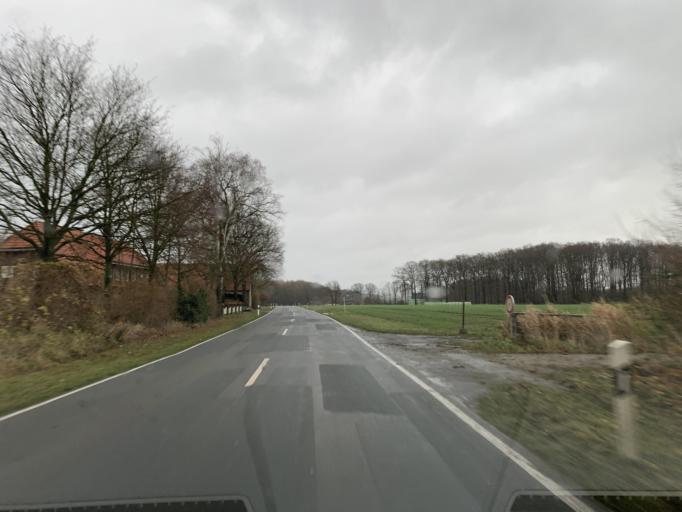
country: DE
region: North Rhine-Westphalia
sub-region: Regierungsbezirk Munster
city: Nordwalde
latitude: 52.1236
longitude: 7.4165
